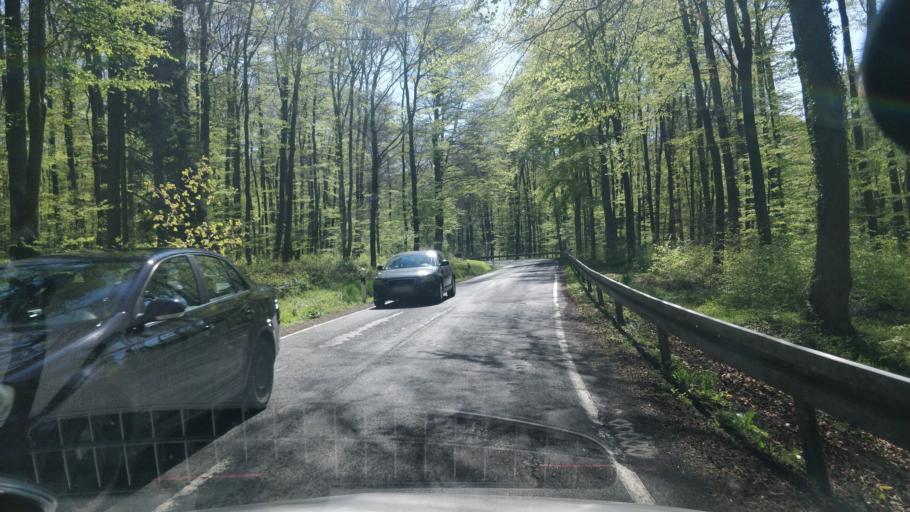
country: DE
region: Rheinland-Pfalz
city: Irmtraut
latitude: 50.5298
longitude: 8.0652
